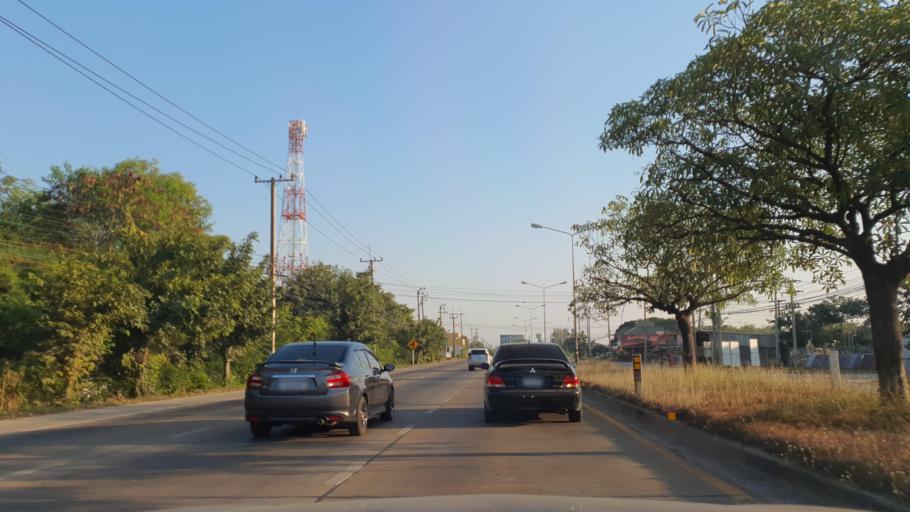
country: TH
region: Phitsanulok
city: Phitsanulok
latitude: 16.8564
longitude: 100.2180
